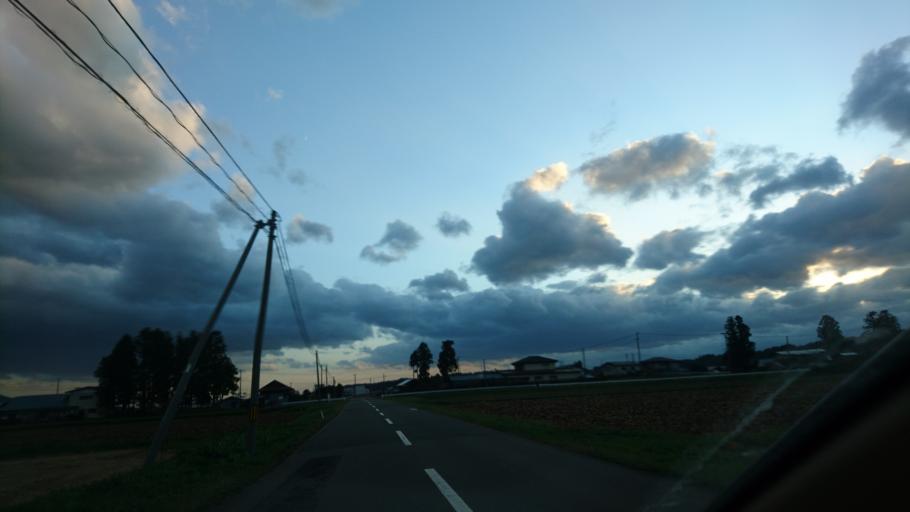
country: JP
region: Iwate
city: Mizusawa
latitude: 39.1052
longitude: 141.1486
